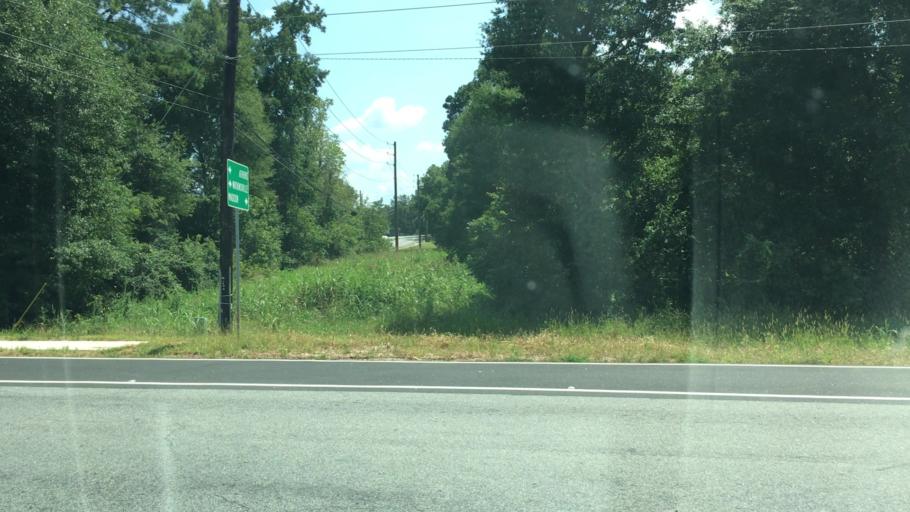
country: US
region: Georgia
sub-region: Oconee County
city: Watkinsville
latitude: 33.8243
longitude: -83.4412
